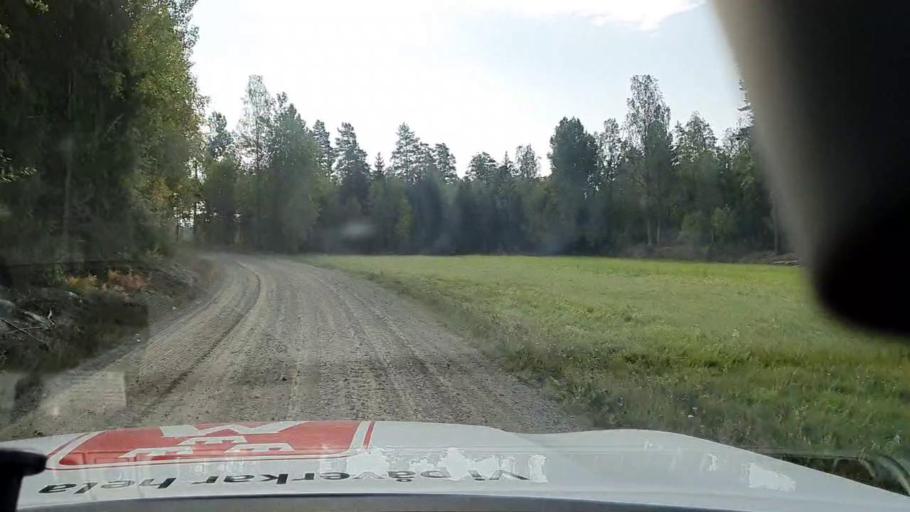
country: SE
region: Vaestmanland
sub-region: Kungsors Kommun
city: Kungsoer
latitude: 59.3587
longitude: 16.1483
